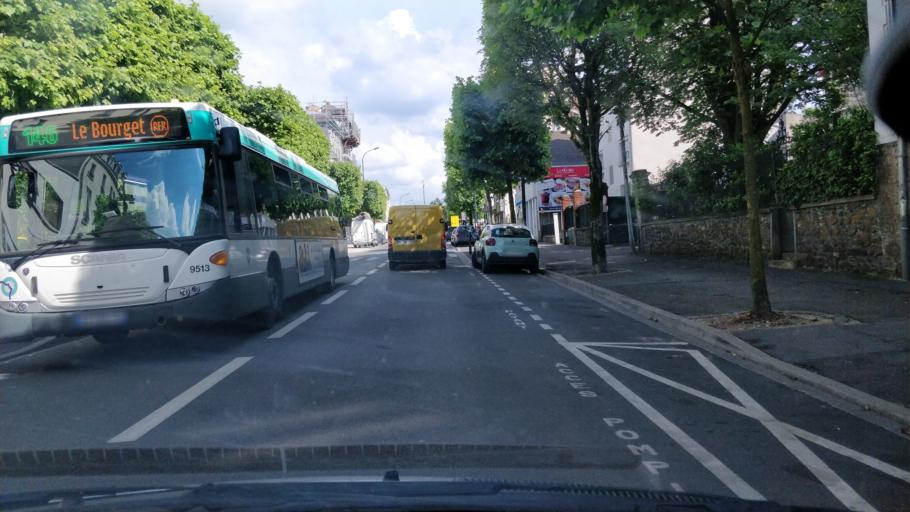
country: FR
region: Ile-de-France
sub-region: Departement de Seine-Saint-Denis
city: Le Raincy
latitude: 48.8999
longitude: 2.5157
